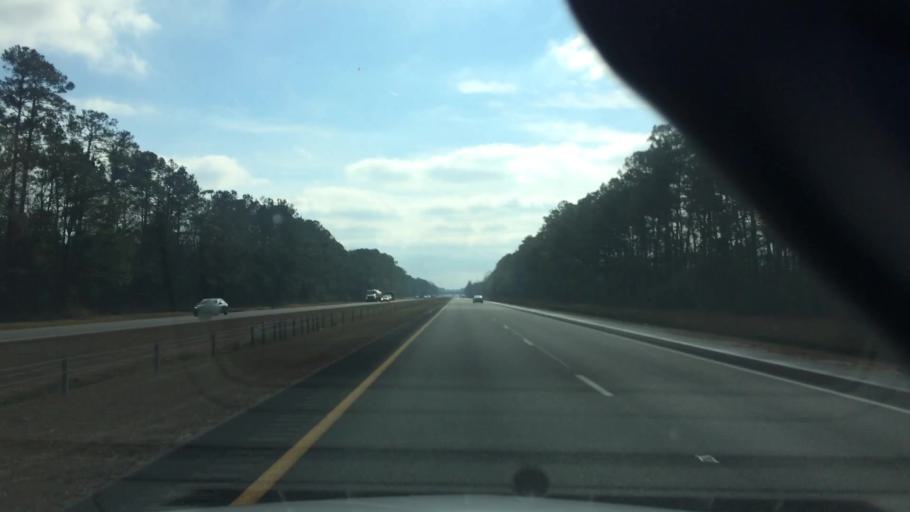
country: US
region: North Carolina
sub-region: Pender County
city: Rocky Point
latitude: 34.4943
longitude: -77.8773
